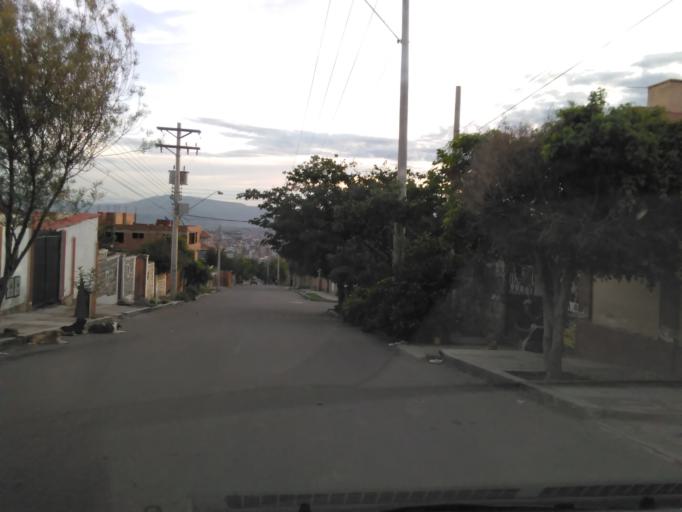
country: BO
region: Cochabamba
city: Cochabamba
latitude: -17.3556
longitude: -66.1598
